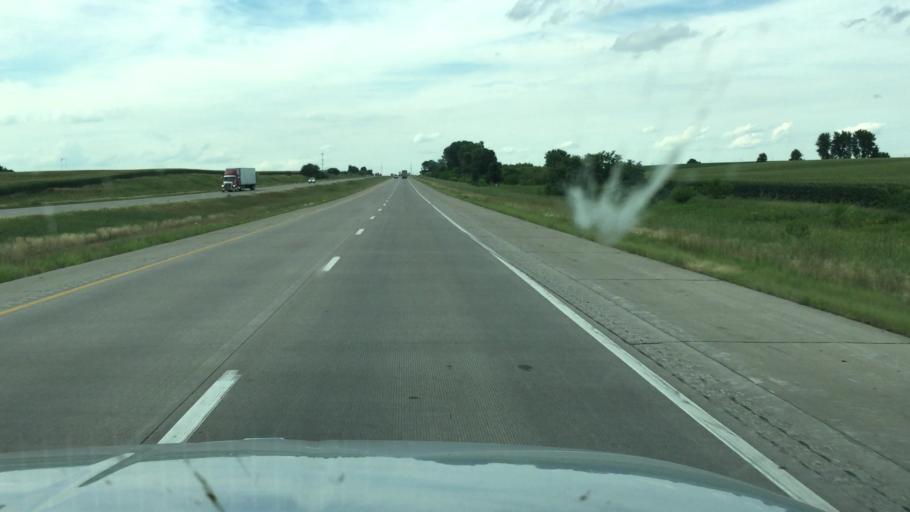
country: US
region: Iowa
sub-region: Scott County
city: Walcott
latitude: 41.5562
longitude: -90.6781
